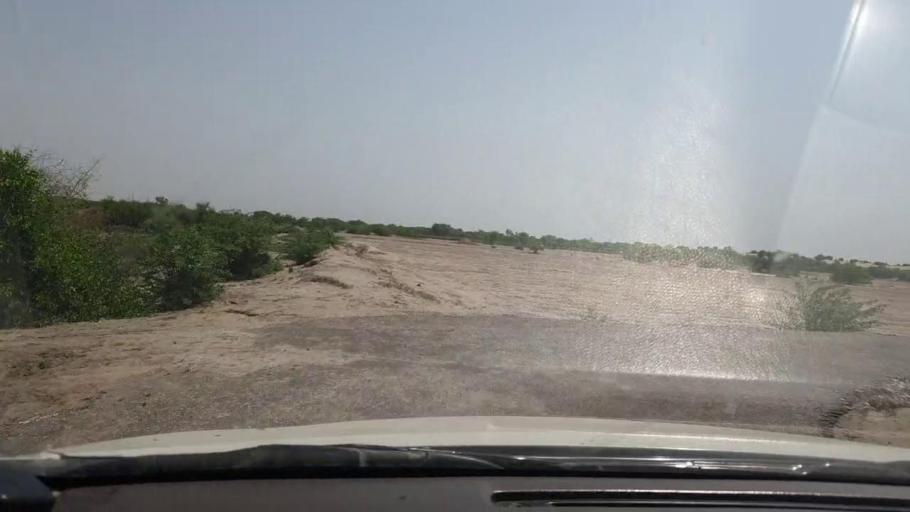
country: PK
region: Sindh
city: Rohri
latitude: 27.5185
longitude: 69.0883
